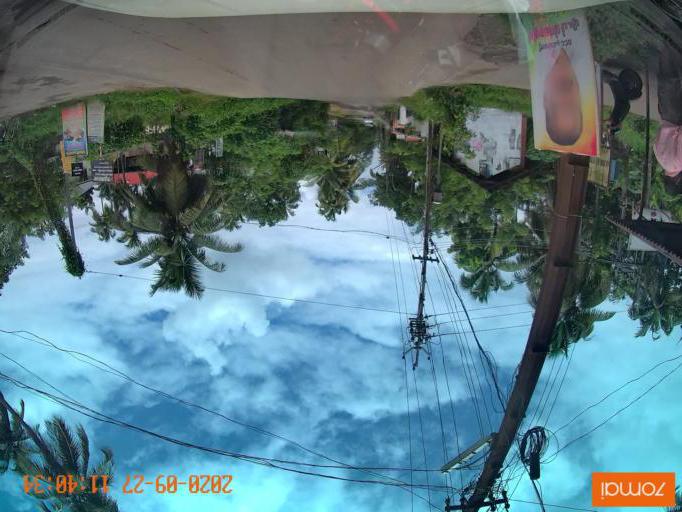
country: IN
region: Kerala
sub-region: Thrissur District
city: Thanniyam
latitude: 10.4694
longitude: 76.1165
